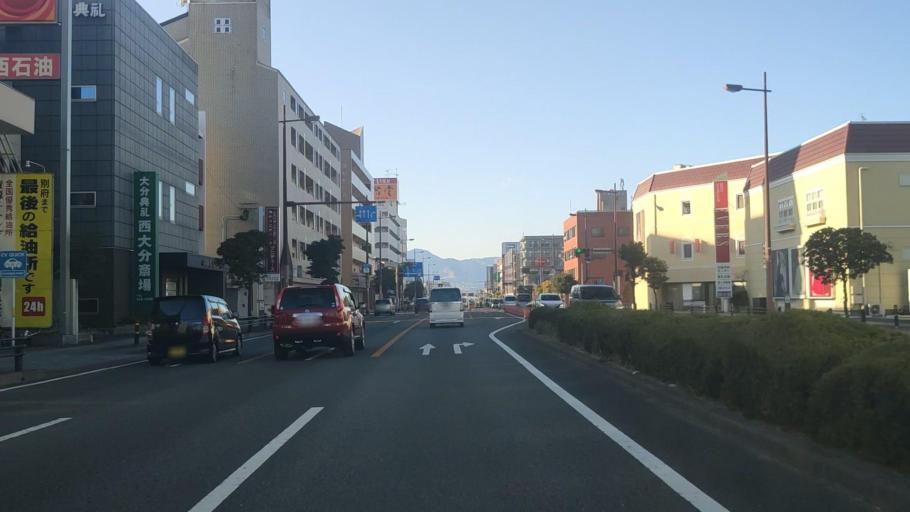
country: JP
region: Oita
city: Oita
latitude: 33.2425
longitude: 131.5905
